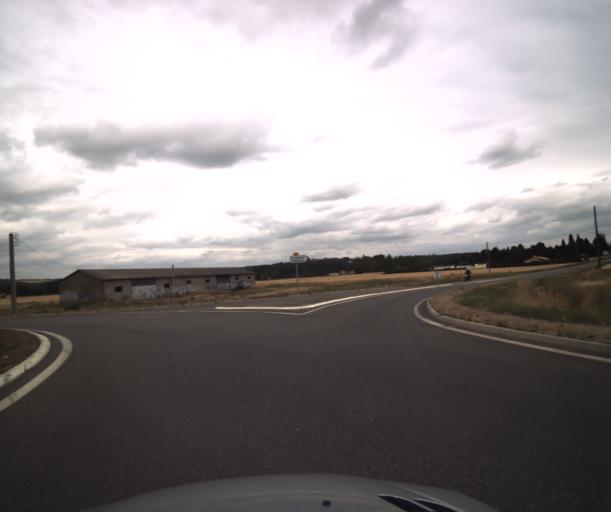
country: FR
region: Midi-Pyrenees
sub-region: Departement de la Haute-Garonne
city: Vernet
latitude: 43.4417
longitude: 1.4160
